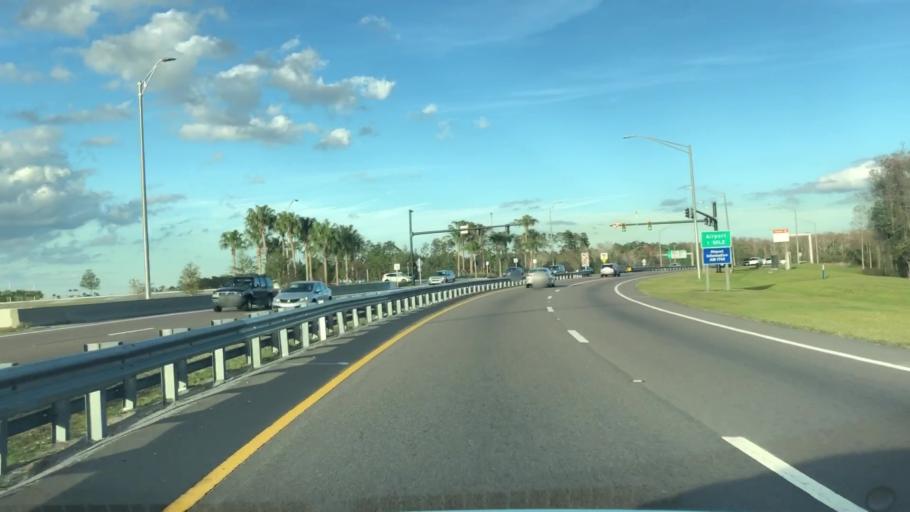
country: US
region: Florida
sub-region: Orange County
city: Taft
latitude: 28.4073
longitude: -81.3071
